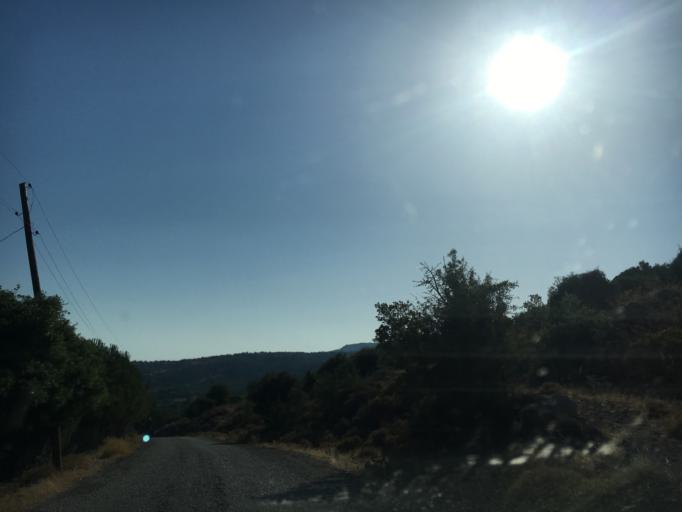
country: TR
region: Canakkale
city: Behram
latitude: 39.4852
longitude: 26.2664
